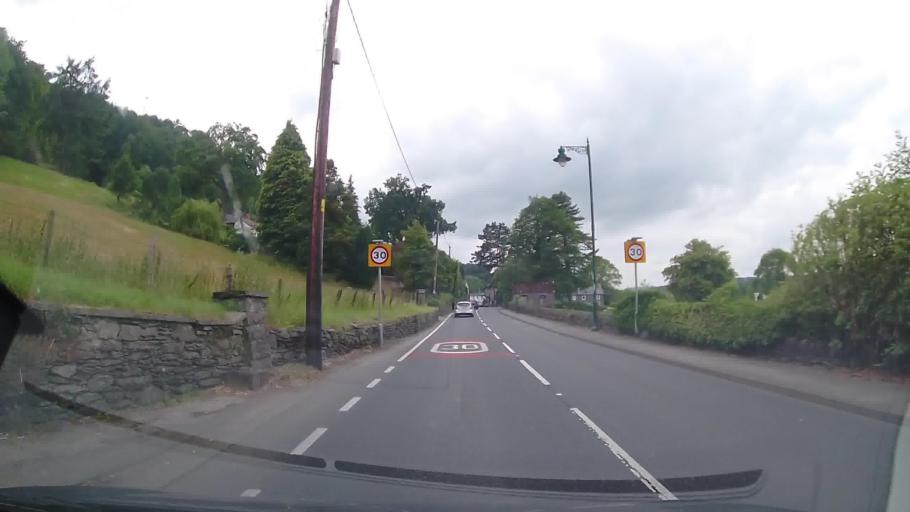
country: GB
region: Wales
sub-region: Denbighshire
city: Corwen
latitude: 52.9811
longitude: -3.3672
